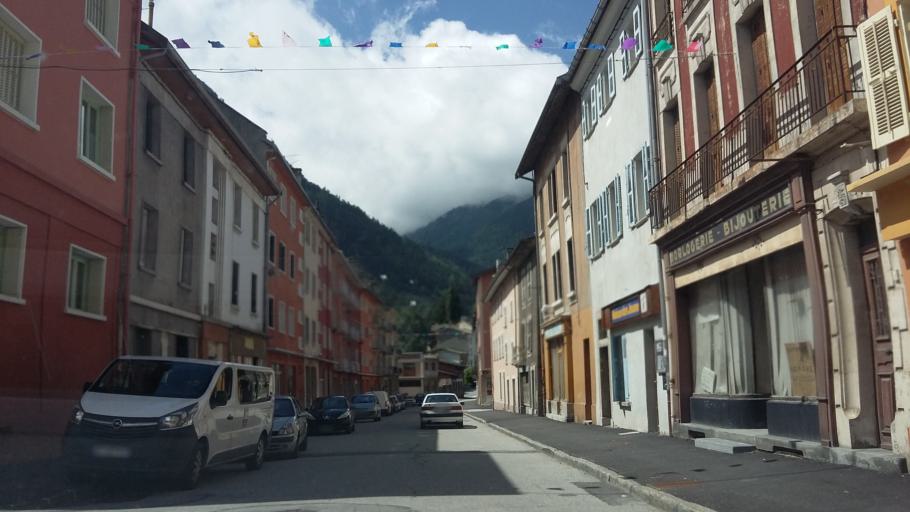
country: FR
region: Rhone-Alpes
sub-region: Departement de la Savoie
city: Modane
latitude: 45.2016
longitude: 6.6726
